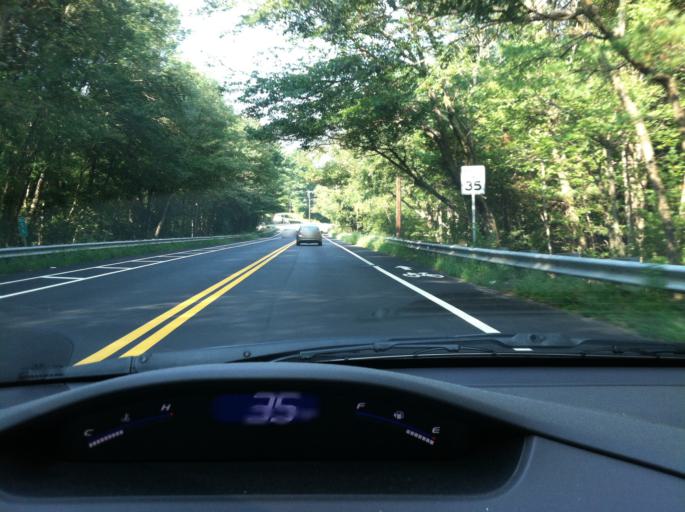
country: US
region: Massachusetts
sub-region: Middlesex County
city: Pinehurst
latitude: 42.5017
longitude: -71.2454
